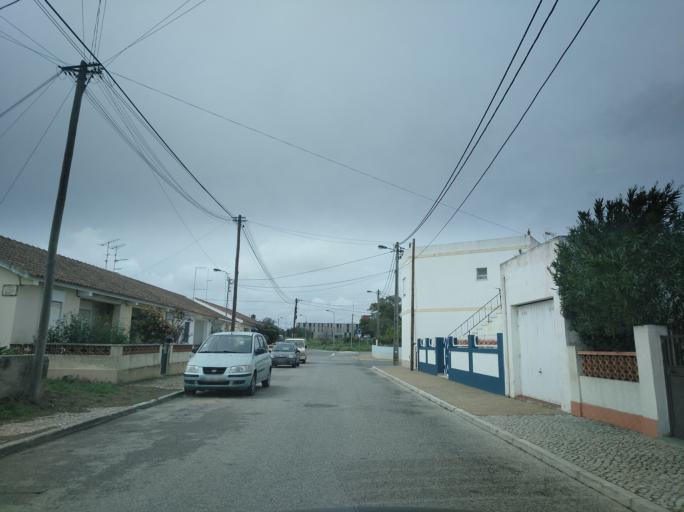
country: PT
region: Setubal
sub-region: Grandola
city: Grandola
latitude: 38.1795
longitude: -8.5717
